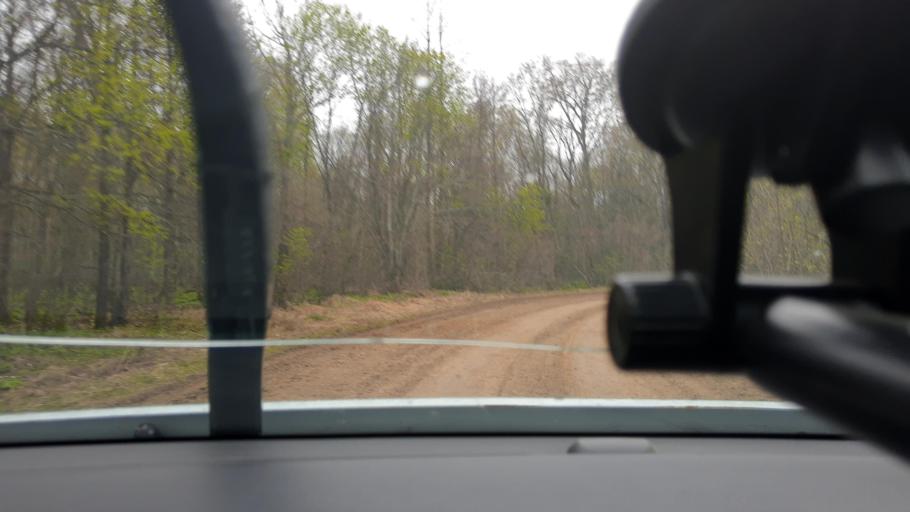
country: RU
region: Bashkortostan
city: Pavlovka
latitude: 55.4302
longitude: 56.3506
